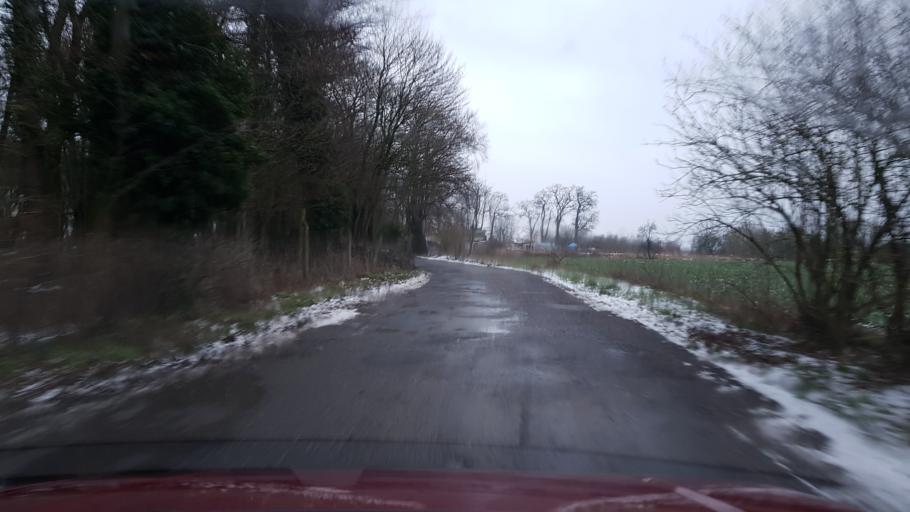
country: PL
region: West Pomeranian Voivodeship
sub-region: Powiat goleniowski
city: Mosty
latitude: 53.5007
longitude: 14.9420
